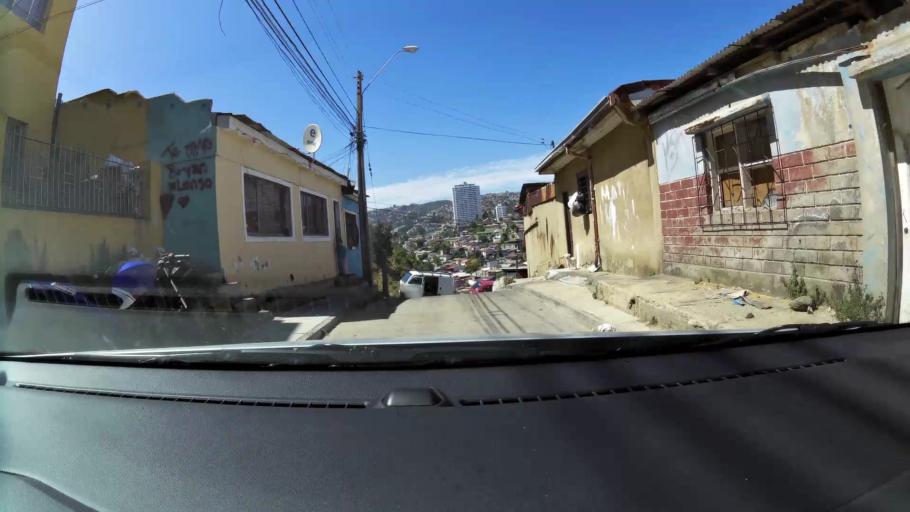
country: CL
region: Valparaiso
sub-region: Provincia de Valparaiso
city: Valparaiso
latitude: -33.0511
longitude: -71.5956
